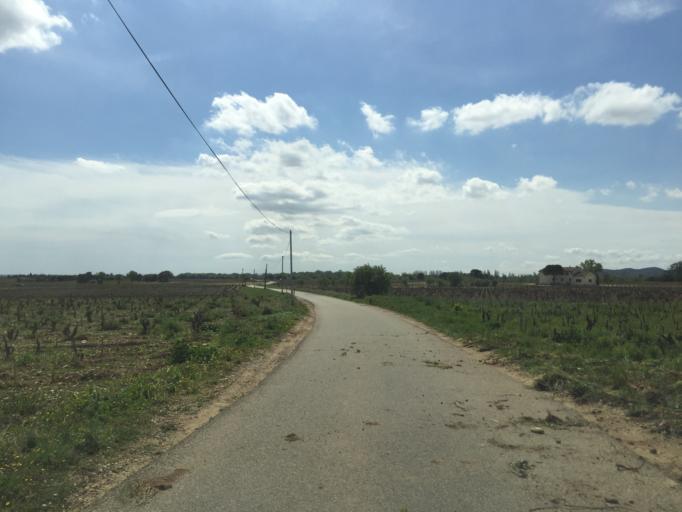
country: FR
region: Provence-Alpes-Cote d'Azur
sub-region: Departement du Vaucluse
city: Chateauneuf-du-Pape
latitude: 44.0450
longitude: 4.8358
